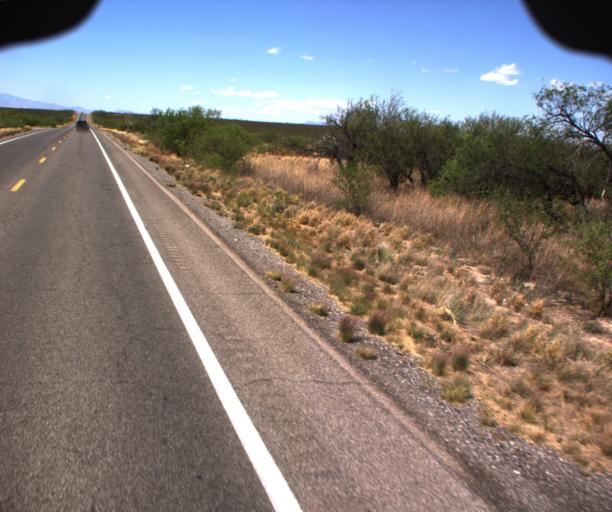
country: US
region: Arizona
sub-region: Cochise County
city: Saint David
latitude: 31.7997
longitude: -110.1571
